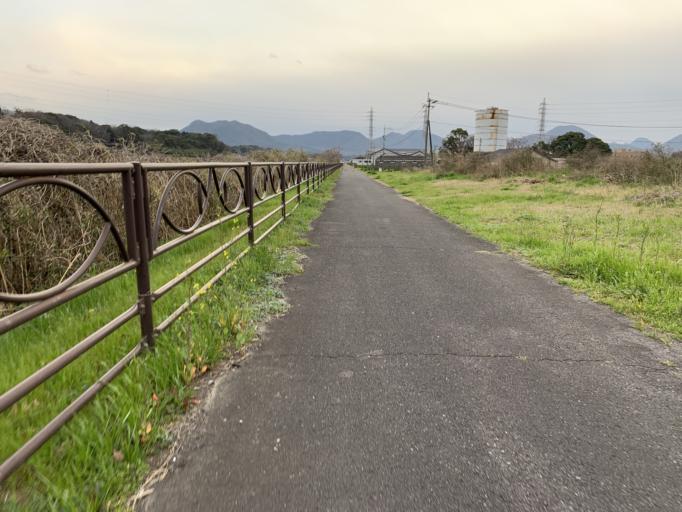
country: JP
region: Oita
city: Bungo-Takada-shi
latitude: 33.5381
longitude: 131.3530
